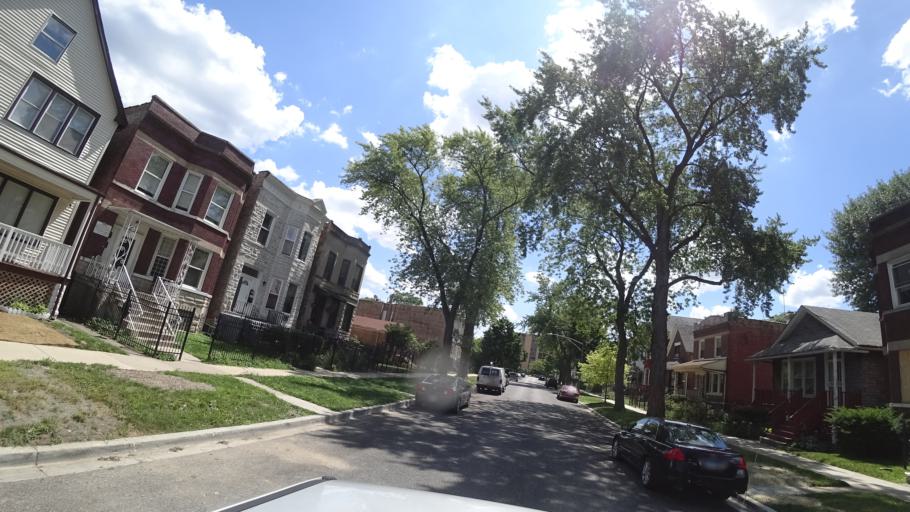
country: US
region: Illinois
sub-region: Cook County
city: Chicago
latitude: 41.7710
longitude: -87.6082
